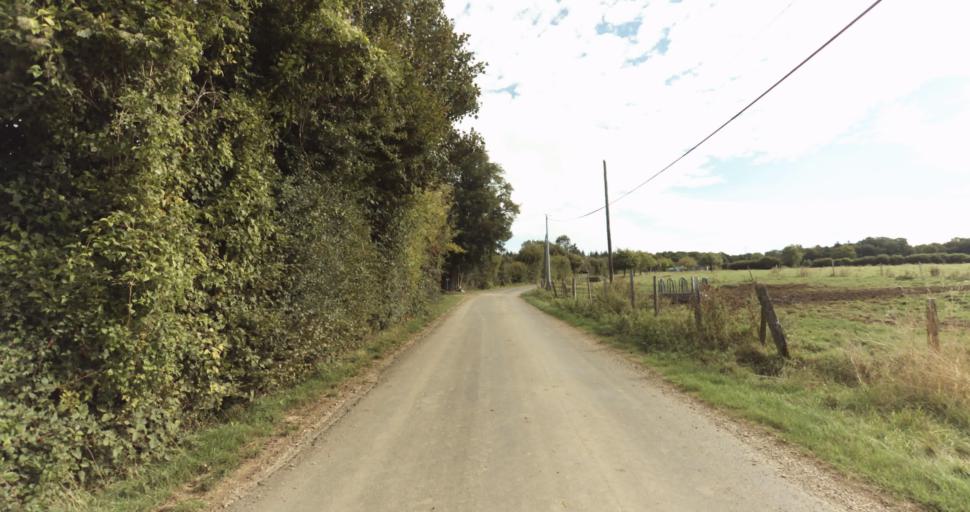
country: FR
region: Lower Normandy
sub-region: Departement de l'Orne
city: Gace
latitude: 48.8149
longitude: 0.2309
